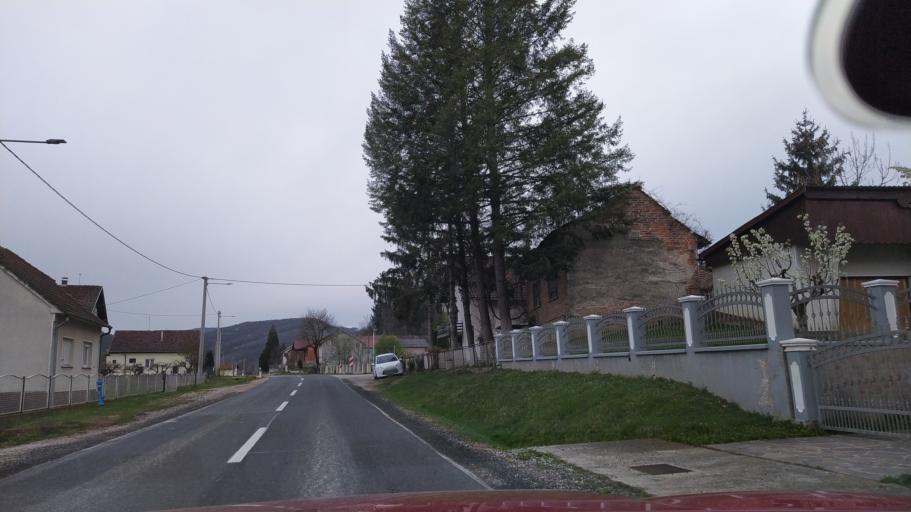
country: HR
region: Varazdinska
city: Ludbreg
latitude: 46.2267
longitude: 16.5440
